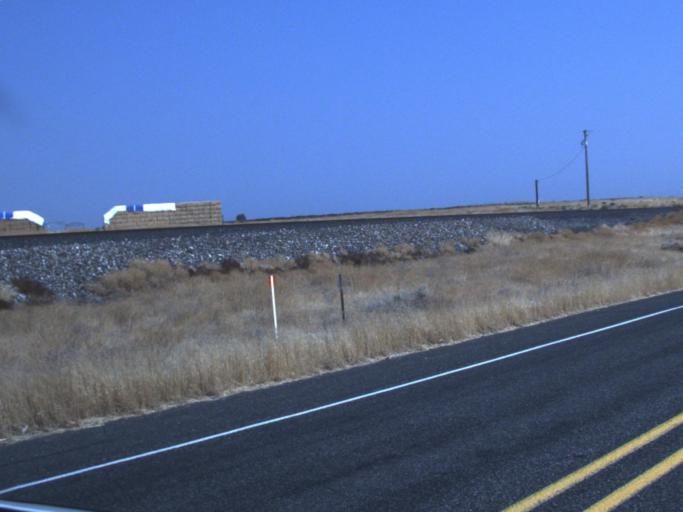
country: US
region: Washington
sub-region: Yakima County
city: Mabton
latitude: 46.2266
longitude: -120.0599
